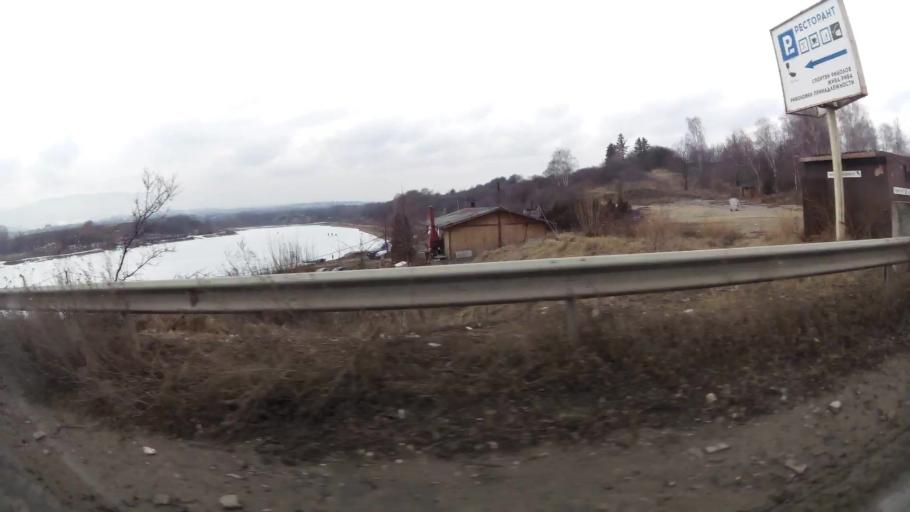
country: BG
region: Sofiya
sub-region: Obshtina Bozhurishte
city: Bozhurishte
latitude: 42.7087
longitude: 23.2303
